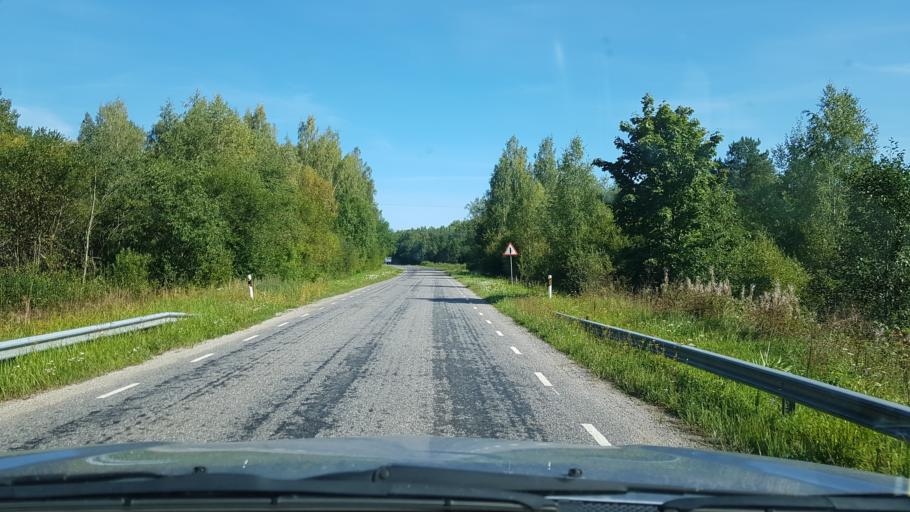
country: EE
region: Ida-Virumaa
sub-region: Sillamaee linn
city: Sillamae
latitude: 59.3511
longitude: 27.7416
